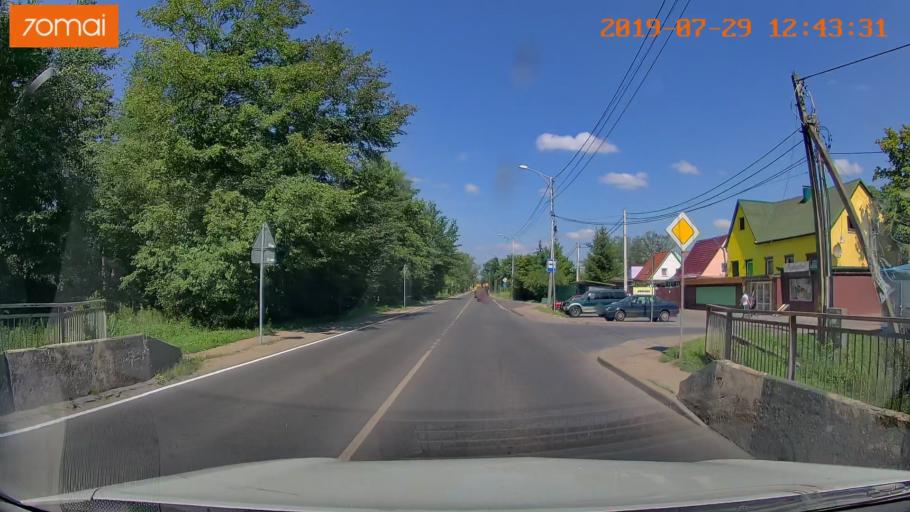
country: RU
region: Kaliningrad
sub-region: Gorod Kaliningrad
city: Kaliningrad
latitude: 54.6769
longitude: 20.5399
